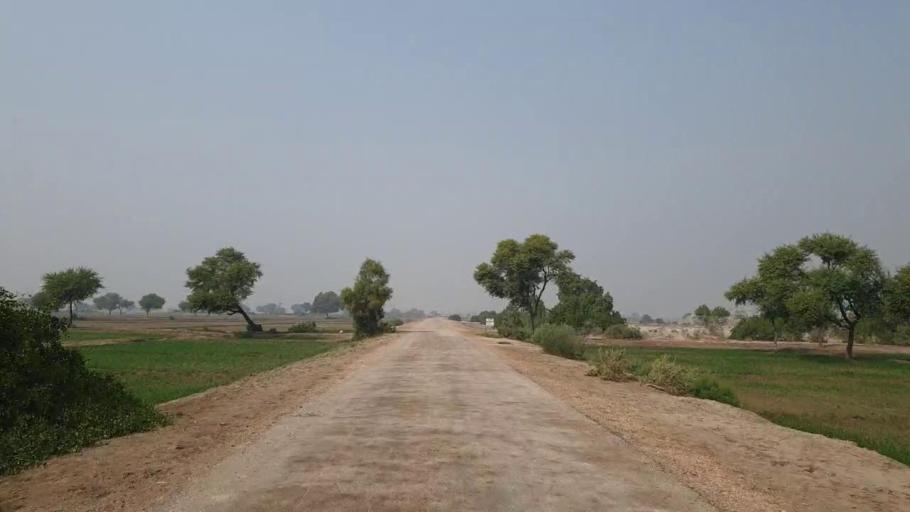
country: PK
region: Sindh
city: Bhan
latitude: 26.4990
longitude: 67.6962
